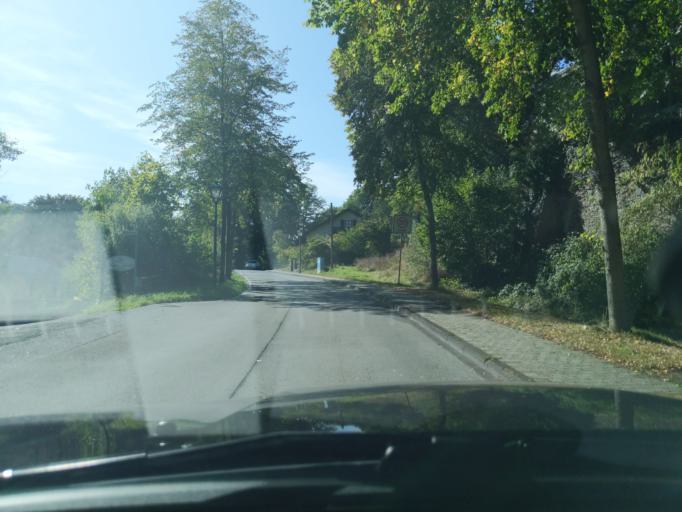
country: DE
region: North Rhine-Westphalia
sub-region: Regierungsbezirk Koln
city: Eitorf
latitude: 50.7649
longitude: 7.3982
